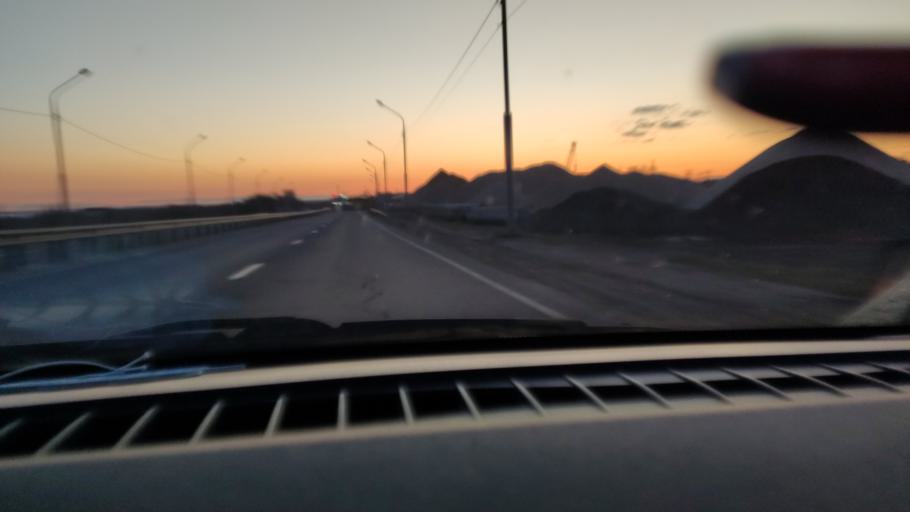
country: RU
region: Saratov
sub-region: Saratovskiy Rayon
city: Saratov
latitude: 51.6476
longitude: 45.9889
